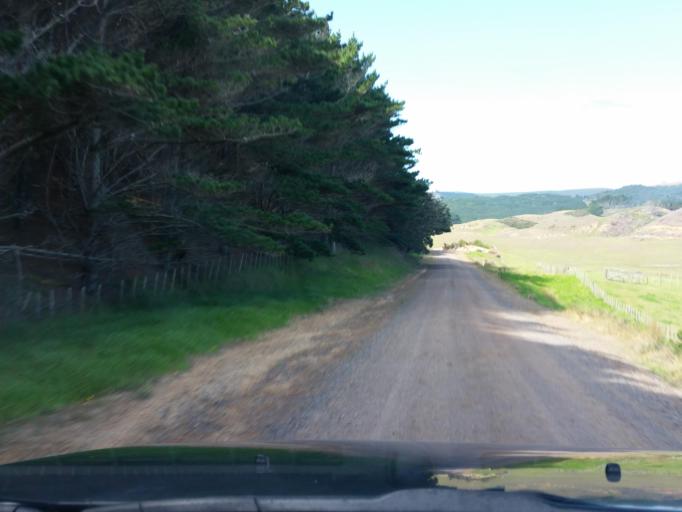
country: NZ
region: Northland
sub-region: Kaipara District
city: Dargaville
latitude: -35.7029
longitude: 173.5245
